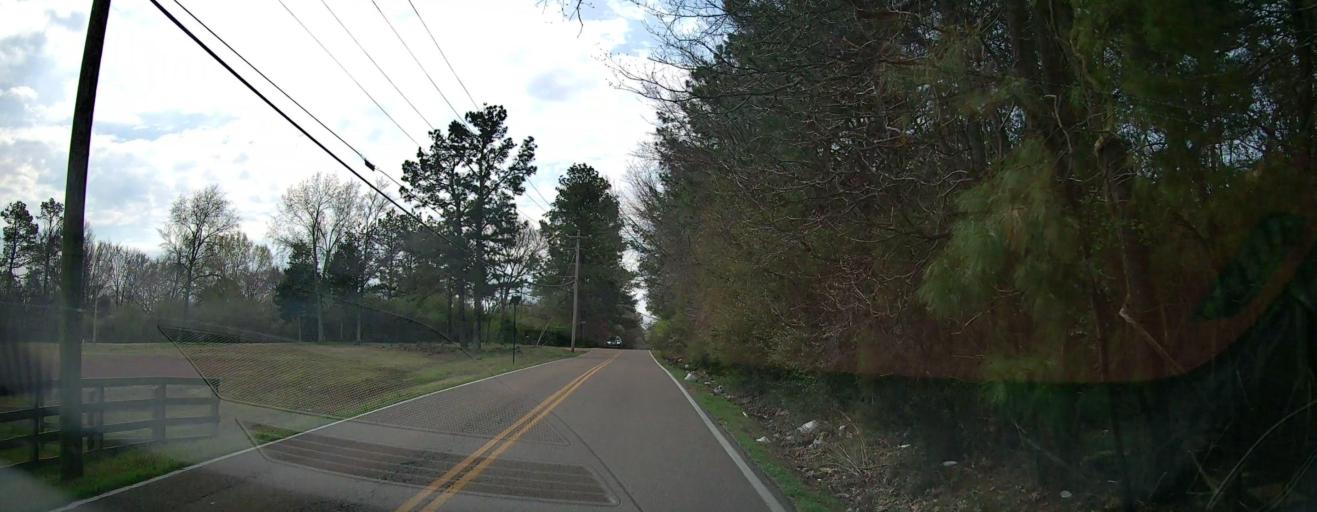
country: US
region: Mississippi
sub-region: De Soto County
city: Olive Branch
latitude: 34.9993
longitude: -89.8484
